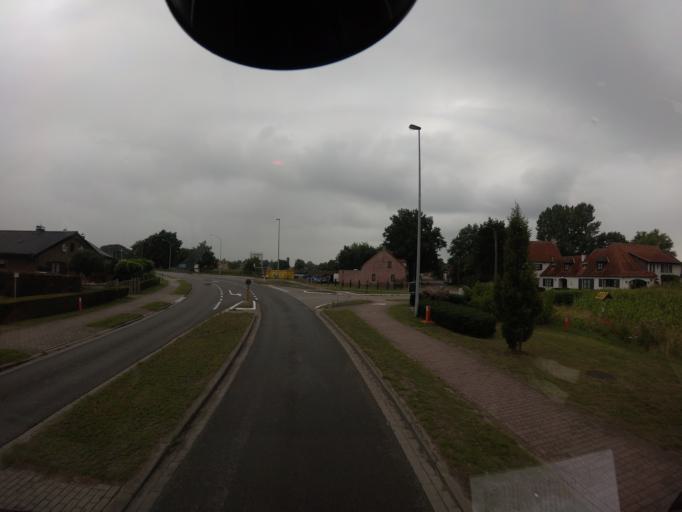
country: BE
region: Flanders
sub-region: Provincie Antwerpen
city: Arendonk
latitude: 51.3413
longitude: 5.1061
